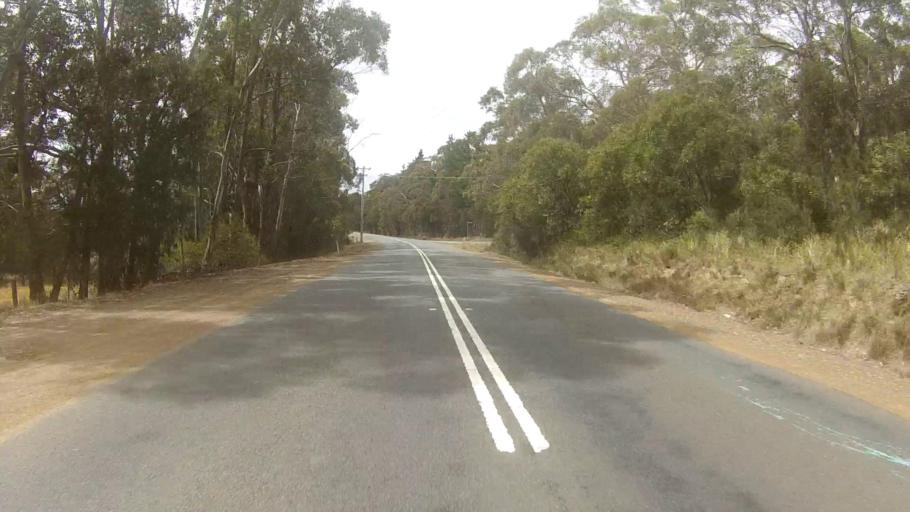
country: AU
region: Tasmania
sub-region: Kingborough
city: Margate
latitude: -43.0035
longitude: 147.2355
